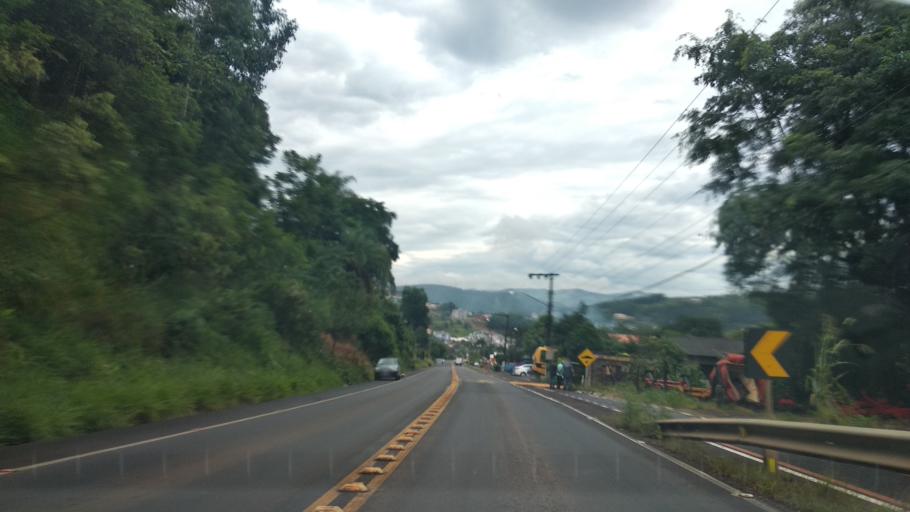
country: BR
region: Santa Catarina
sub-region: Videira
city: Videira
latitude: -27.0906
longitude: -51.2439
